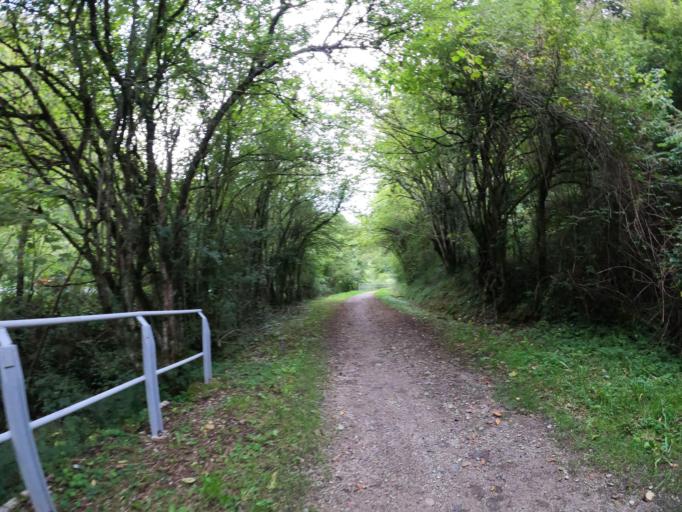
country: ES
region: Navarre
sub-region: Provincia de Navarra
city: Lekunberri
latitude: 43.0262
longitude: -1.9081
